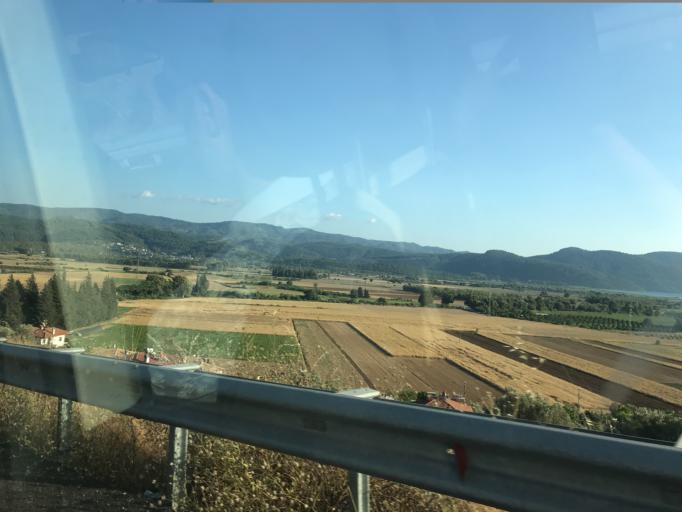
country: TR
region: Mugla
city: Ula
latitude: 37.0555
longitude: 28.3508
